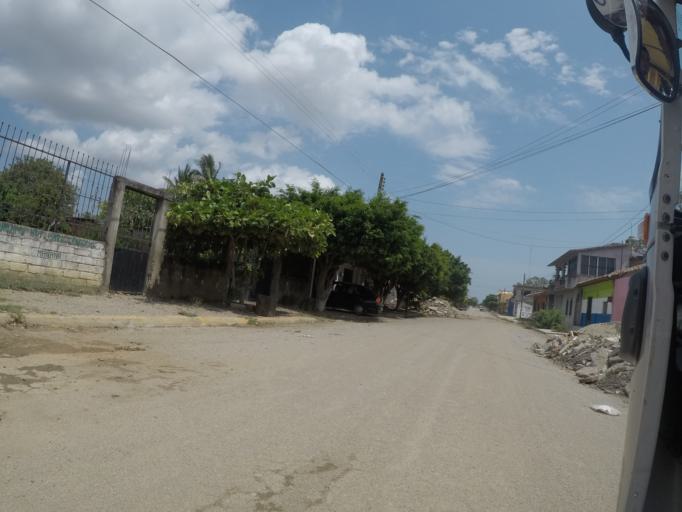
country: MX
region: Oaxaca
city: Union Hidalgo
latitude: 16.4775
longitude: -94.8278
